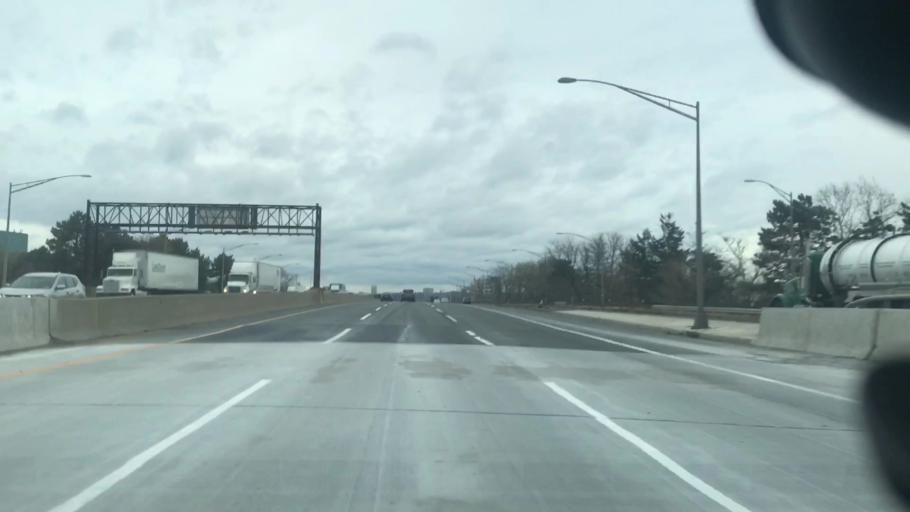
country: US
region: New Jersey
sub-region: Hudson County
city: Secaucus
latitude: 40.7856
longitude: -74.0514
